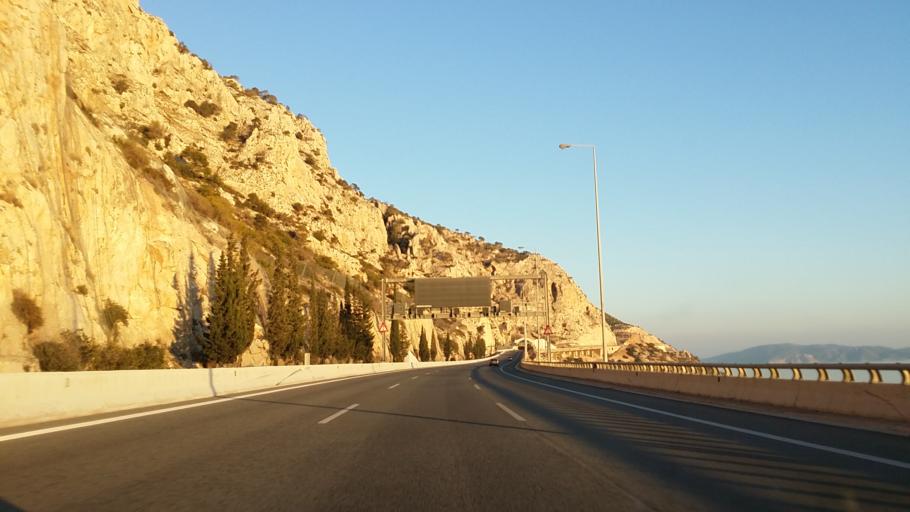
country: GR
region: Attica
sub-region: Nomarchia Dytikis Attikis
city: Kineta
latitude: 37.9793
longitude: 23.2720
